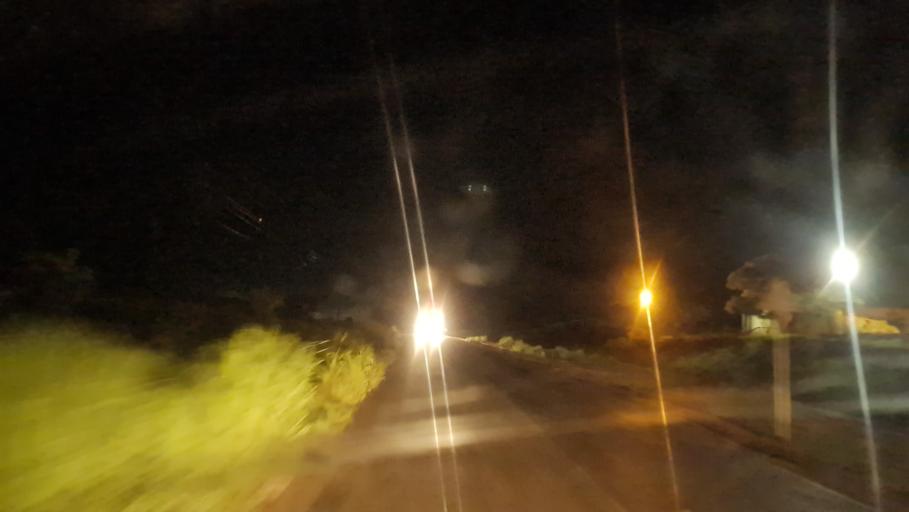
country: MZ
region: Nampula
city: Nacala
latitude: -14.6307
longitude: 40.6703
